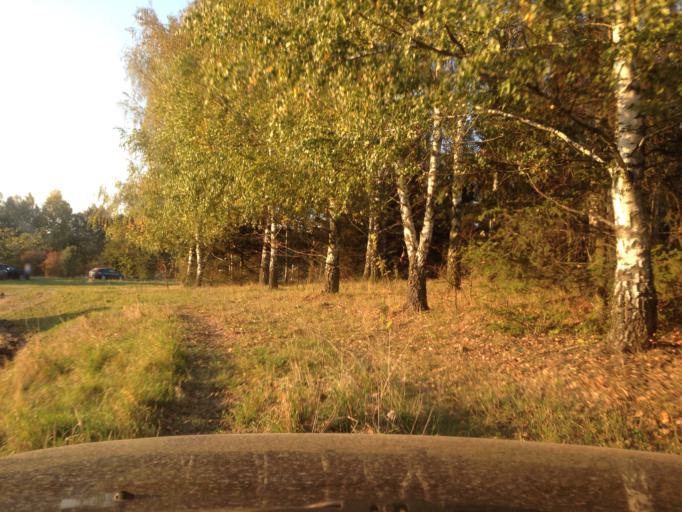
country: PL
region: Kujawsko-Pomorskie
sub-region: Powiat brodnicki
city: Gorzno
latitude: 53.2788
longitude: 19.7107
